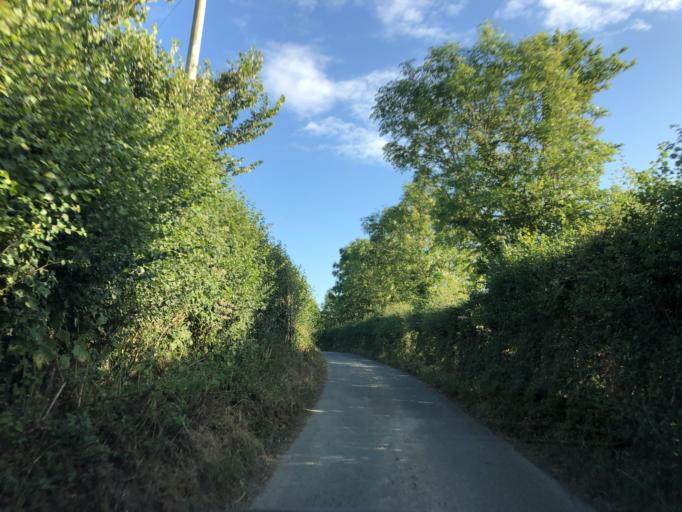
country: GB
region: England
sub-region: Isle of Wight
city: Yarmouth
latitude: 50.6991
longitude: -1.4717
